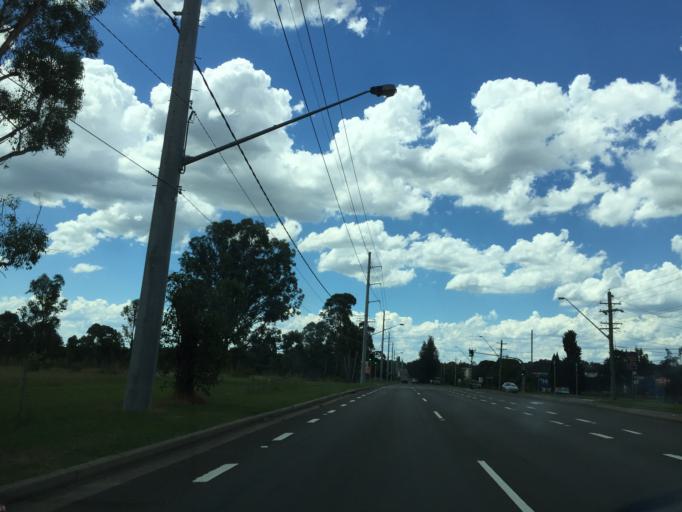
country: AU
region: New South Wales
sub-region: Blacktown
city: Doonside
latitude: -33.7881
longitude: 150.8718
